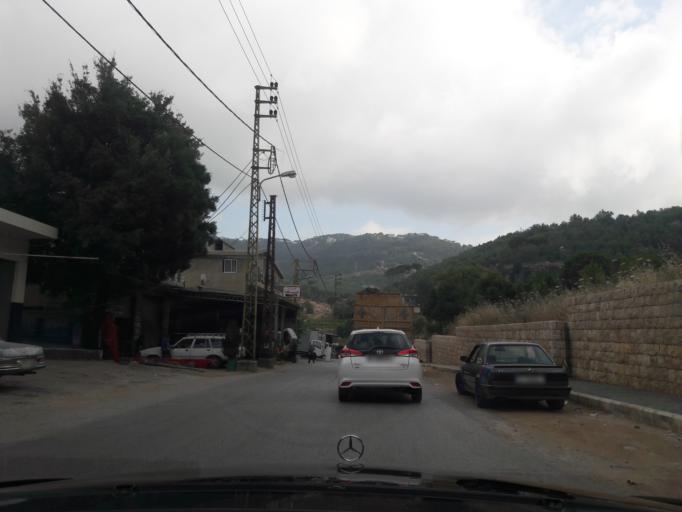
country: LB
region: Mont-Liban
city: Djounie
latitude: 33.9236
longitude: 35.7299
